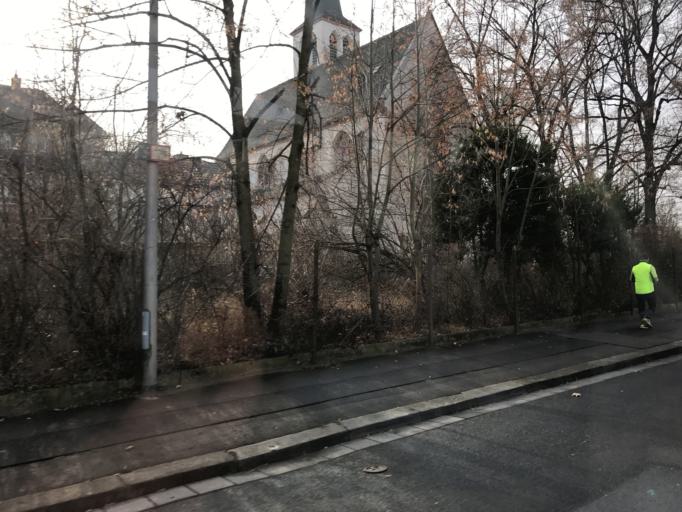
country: DE
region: Rheinland-Pfalz
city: Mainz
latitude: 50.0298
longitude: 8.2592
